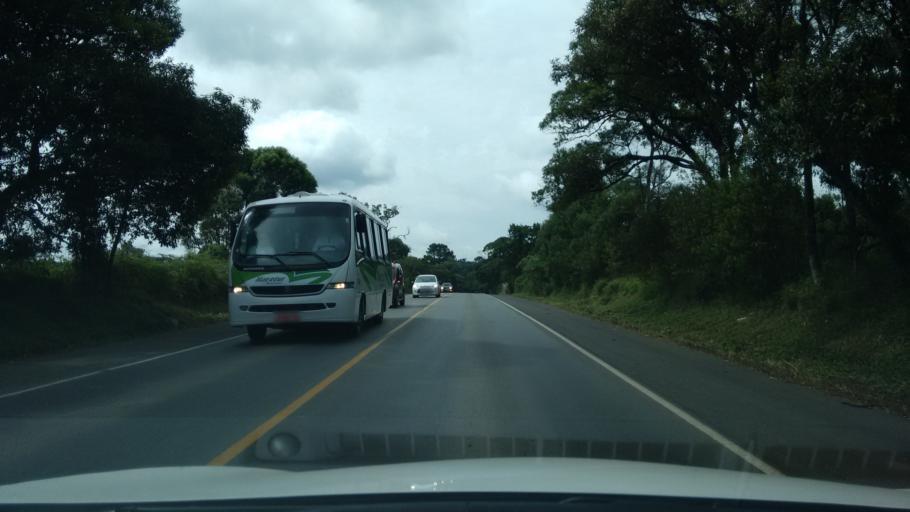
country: BR
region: Santa Catarina
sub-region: Curitibanos
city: Curitibanos
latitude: -27.3103
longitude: -50.3900
